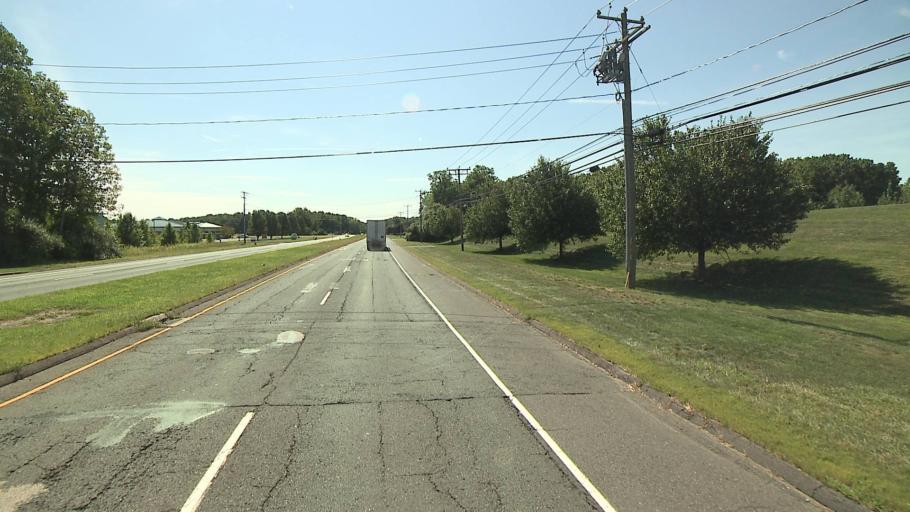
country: US
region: Connecticut
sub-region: Hartford County
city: Blue Hills
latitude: 41.8668
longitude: -72.7194
